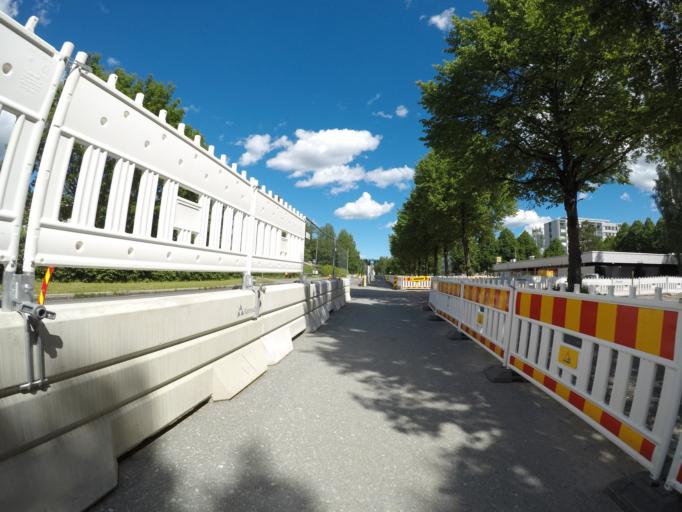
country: FI
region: Haeme
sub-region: Haemeenlinna
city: Haemeenlinna
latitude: 61.0072
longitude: 24.4413
